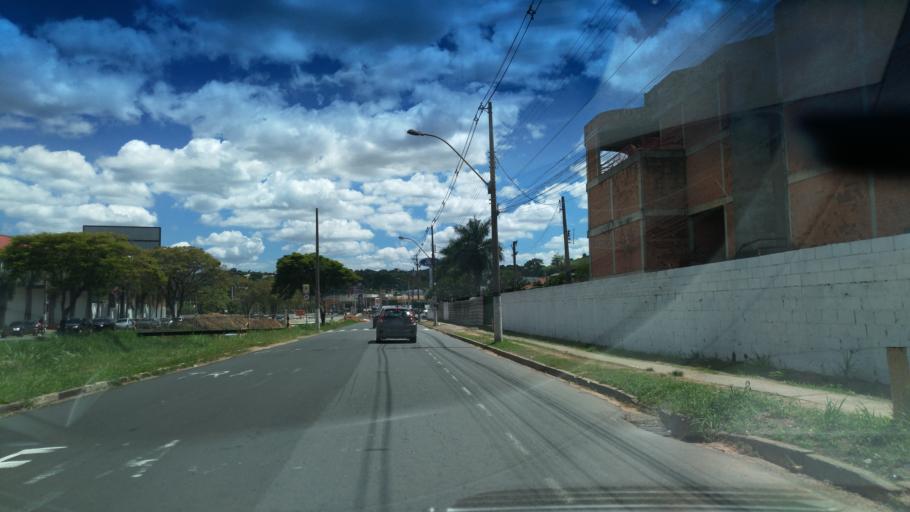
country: BR
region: Sao Paulo
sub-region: Valinhos
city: Valinhos
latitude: -22.9635
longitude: -47.0013
